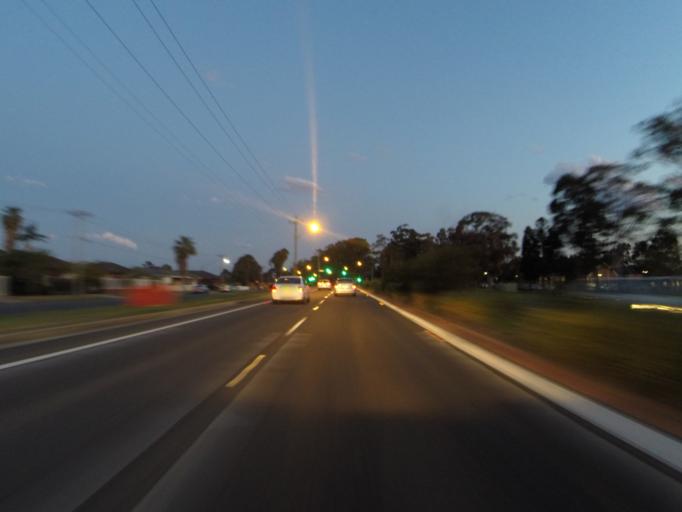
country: AU
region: New South Wales
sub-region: Bankstown
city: Milperra
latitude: -33.9516
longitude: 150.9523
